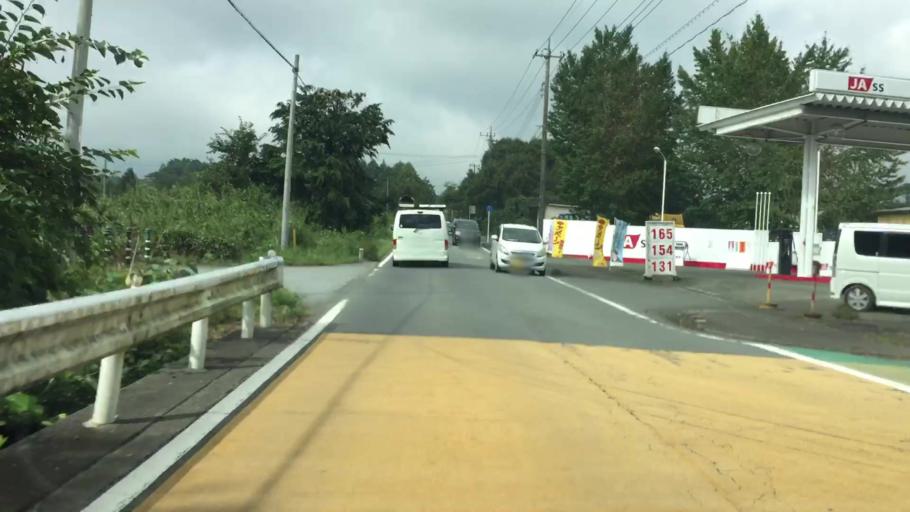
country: JP
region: Shizuoka
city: Fujinomiya
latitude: 35.3430
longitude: 138.5952
